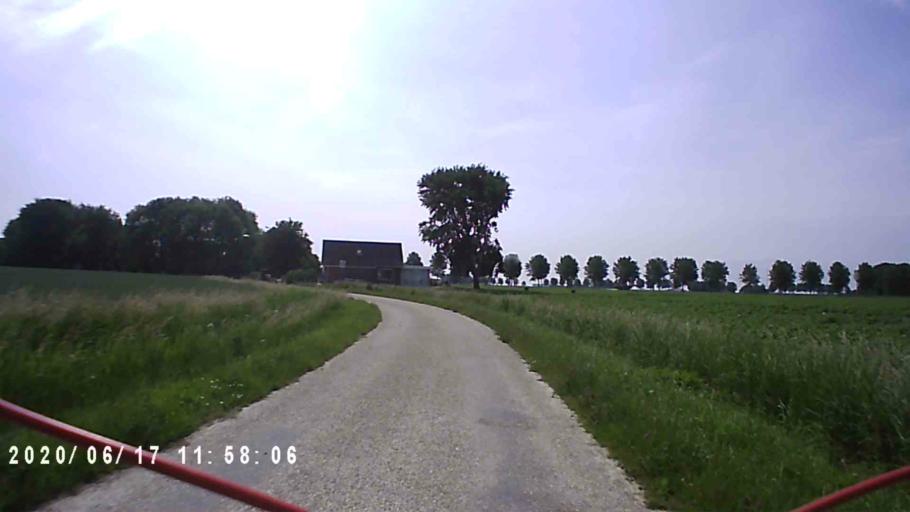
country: NL
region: Groningen
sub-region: Gemeente De Marne
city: Ulrum
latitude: 53.3448
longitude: 6.3268
